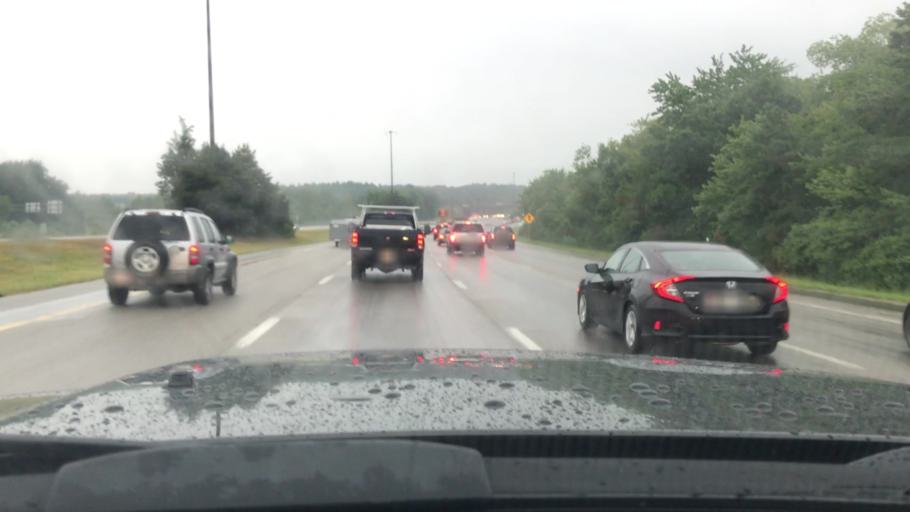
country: US
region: New Hampshire
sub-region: Rockingham County
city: Greenland
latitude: 43.0541
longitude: -70.8090
